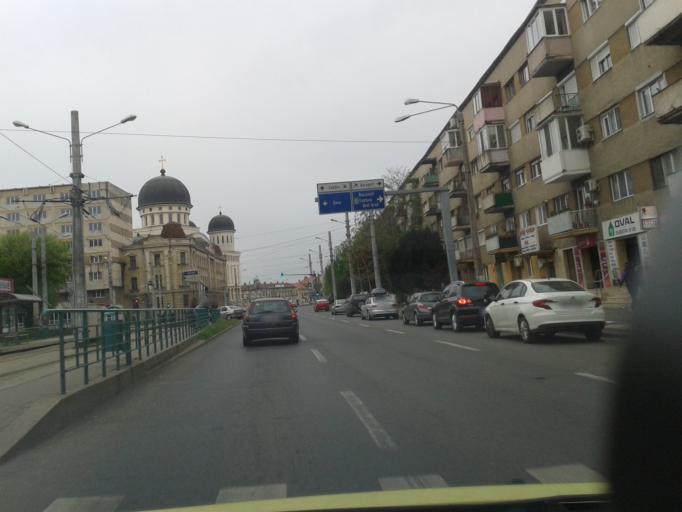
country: RO
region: Arad
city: Arad
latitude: 46.1863
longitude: 21.3253
